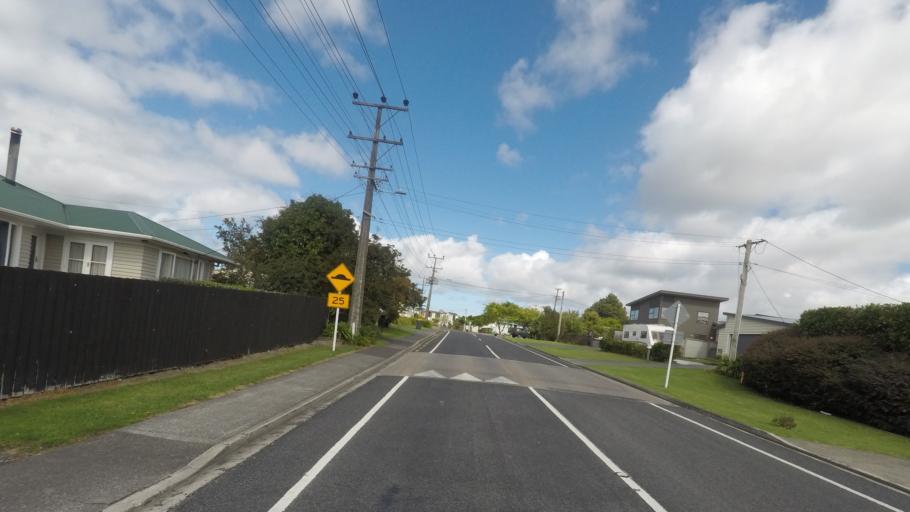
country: NZ
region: Auckland
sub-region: Auckland
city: Muriwai Beach
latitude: -36.7711
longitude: 174.5470
